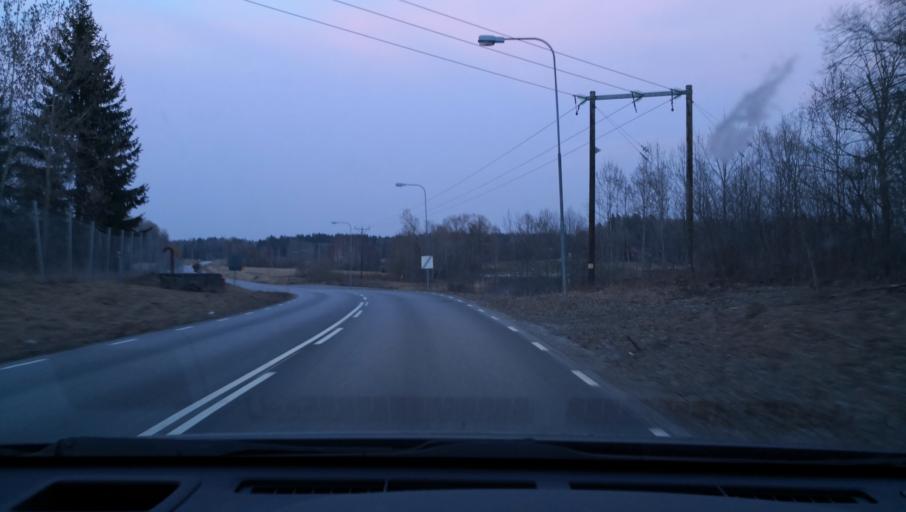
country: SE
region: OErebro
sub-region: Lindesbergs Kommun
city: Lindesberg
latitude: 59.5876
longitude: 15.2539
